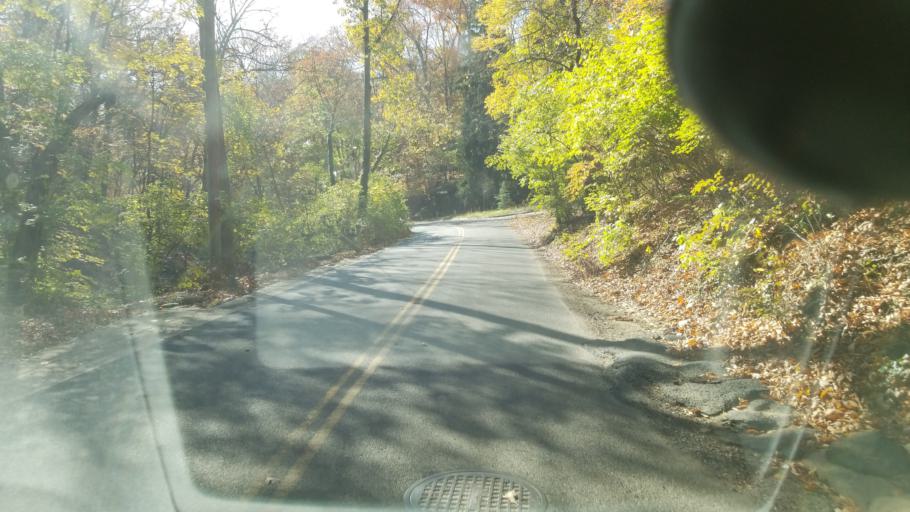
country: US
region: Maryland
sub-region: Montgomery County
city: Chevy Chase
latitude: 38.9513
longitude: -77.0531
